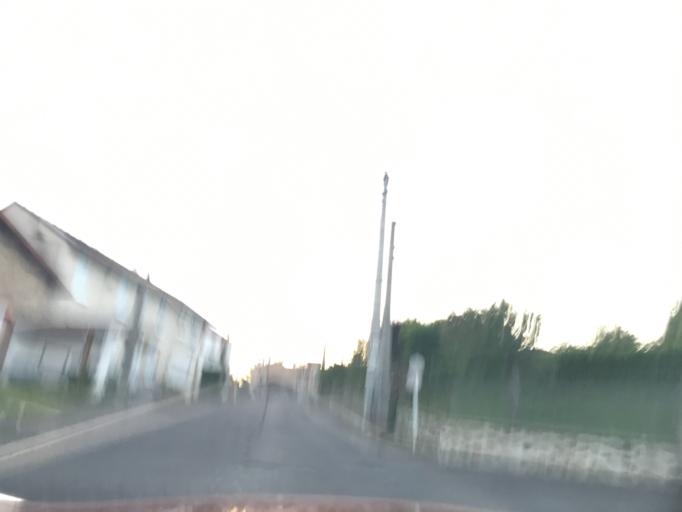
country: FR
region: Auvergne
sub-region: Departement du Puy-de-Dome
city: Saint-Remy-sur-Durolle
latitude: 45.8851
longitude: 3.5920
